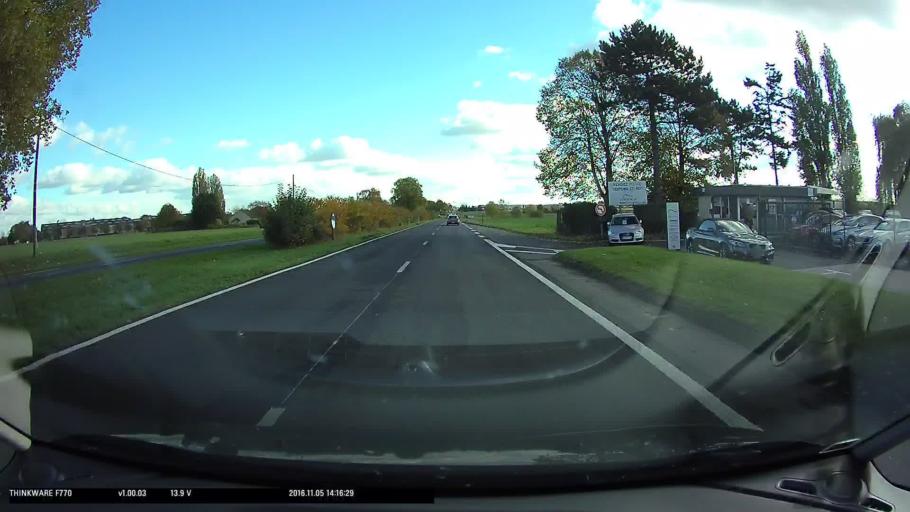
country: FR
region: Ile-de-France
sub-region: Departement du Val-d'Oise
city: Osny
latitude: 49.0834
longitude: 2.0674
